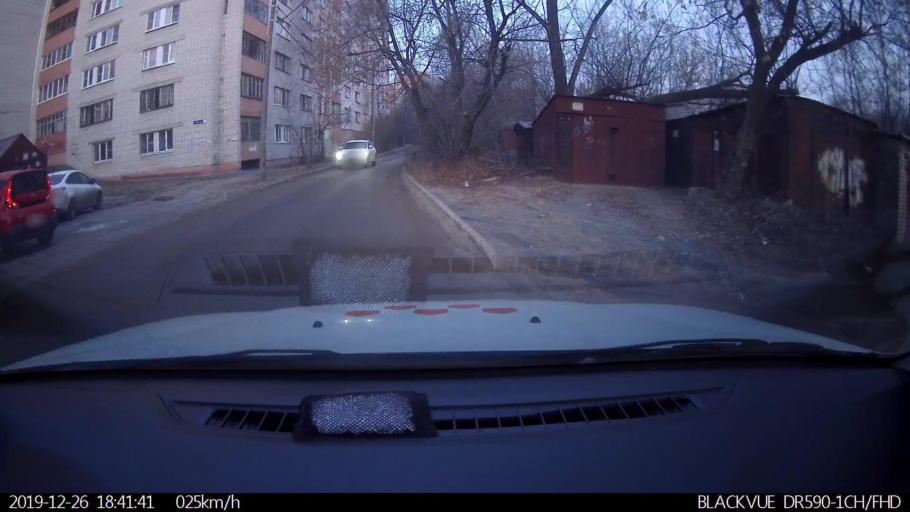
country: RU
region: Nizjnij Novgorod
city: Nizhniy Novgorod
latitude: 56.3165
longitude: 44.0343
